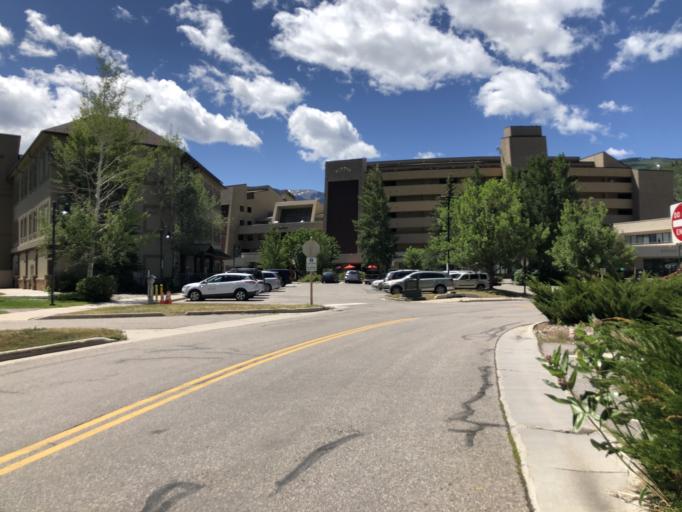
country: US
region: Colorado
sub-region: Eagle County
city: Avon
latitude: 39.6361
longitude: -106.5257
